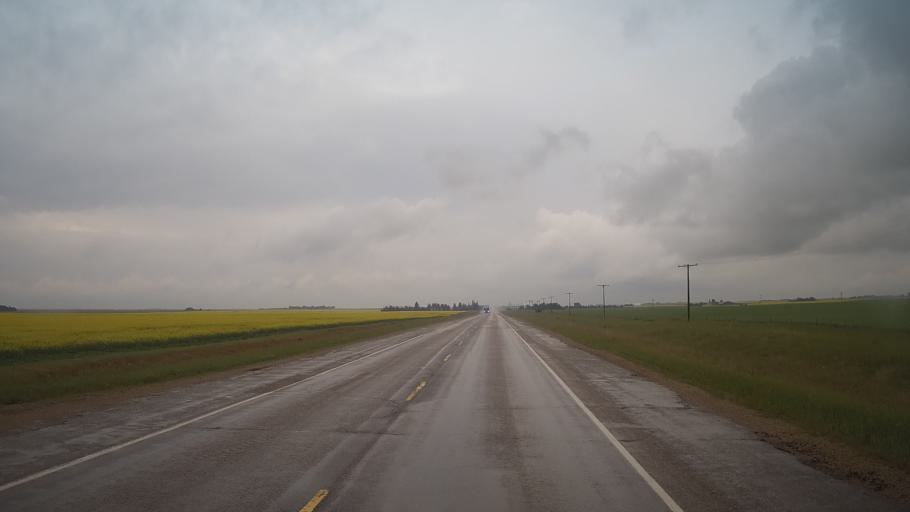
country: CA
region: Saskatchewan
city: Unity
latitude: 52.4349
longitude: -109.0160
